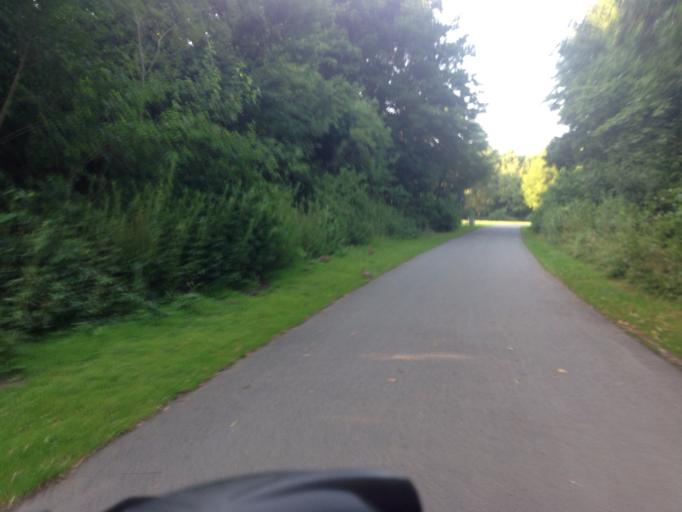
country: DE
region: North Rhine-Westphalia
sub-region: Regierungsbezirk Munster
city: Muenster
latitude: 51.9471
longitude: 7.5955
